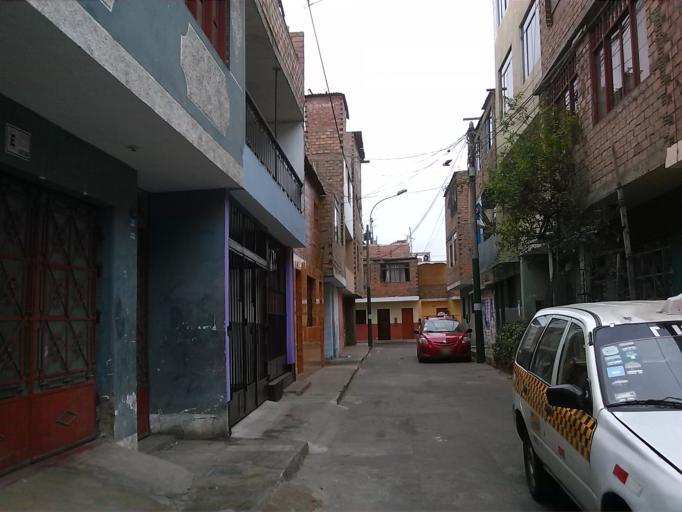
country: PE
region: Callao
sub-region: Callao
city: Callao
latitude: -12.0425
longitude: -77.0981
